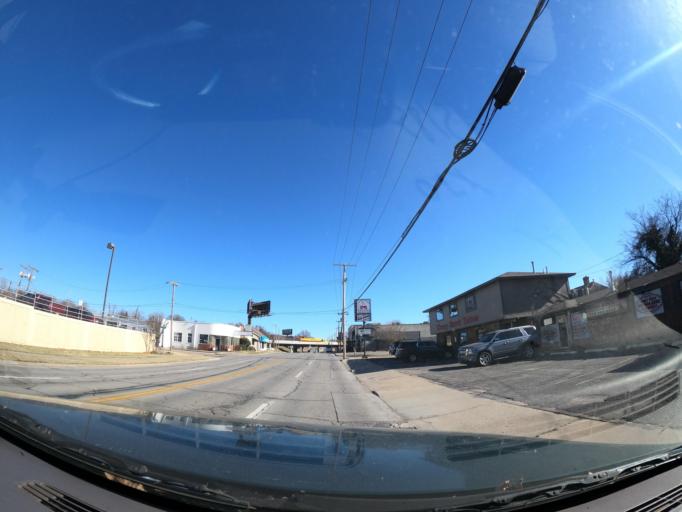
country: US
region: Oklahoma
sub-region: Tulsa County
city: Tulsa
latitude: 36.1405
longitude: -95.9565
